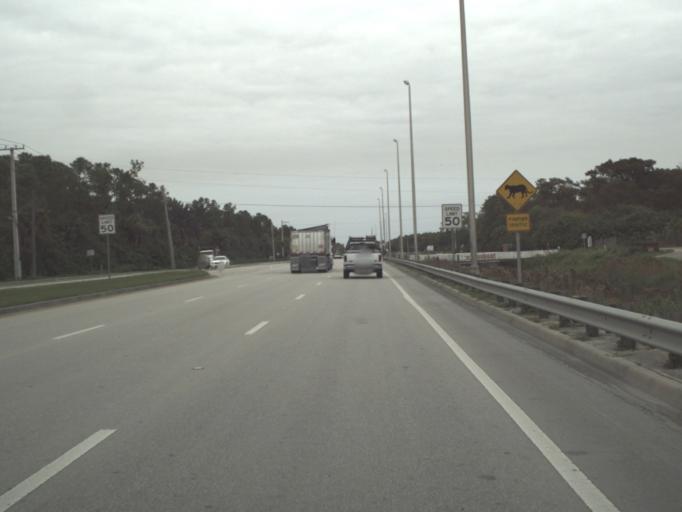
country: US
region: Florida
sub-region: Collier County
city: Lely Resort
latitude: 26.1245
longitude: -81.6869
